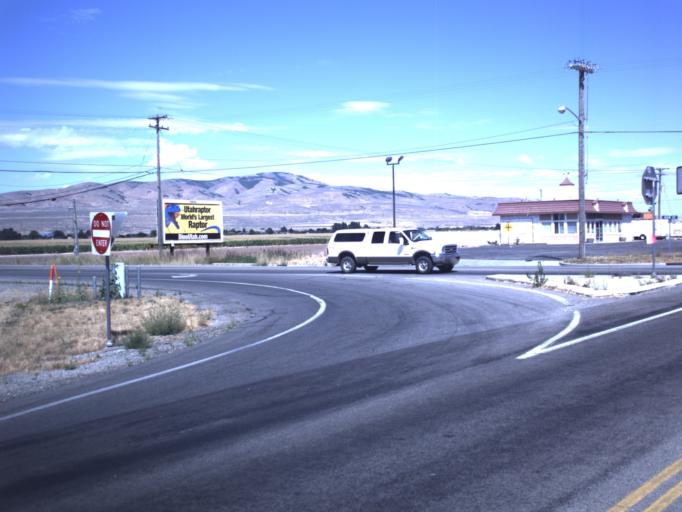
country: US
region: Utah
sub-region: Box Elder County
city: Elwood
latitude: 41.7120
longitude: -112.1422
